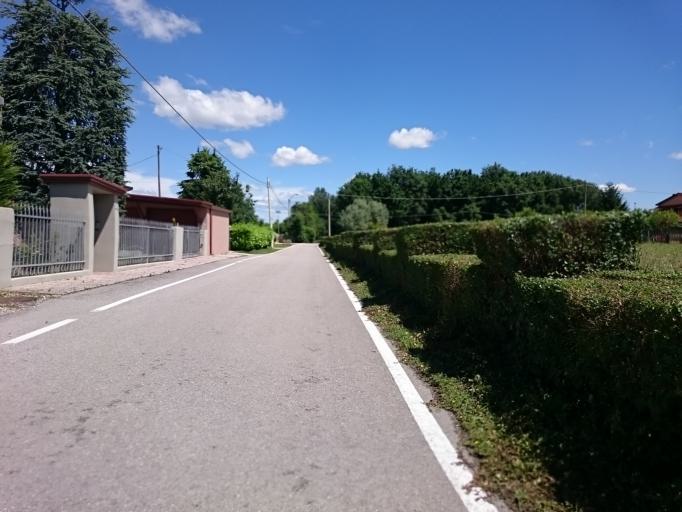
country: IT
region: Veneto
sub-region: Provincia di Padova
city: Polverara
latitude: 45.3094
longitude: 11.9671
